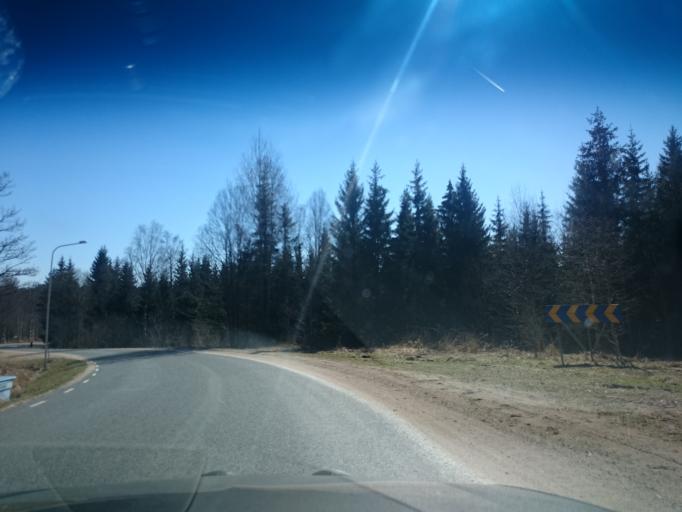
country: SE
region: Kronoberg
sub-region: Vaxjo Kommun
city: Braas
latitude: 57.2387
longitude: 15.0446
